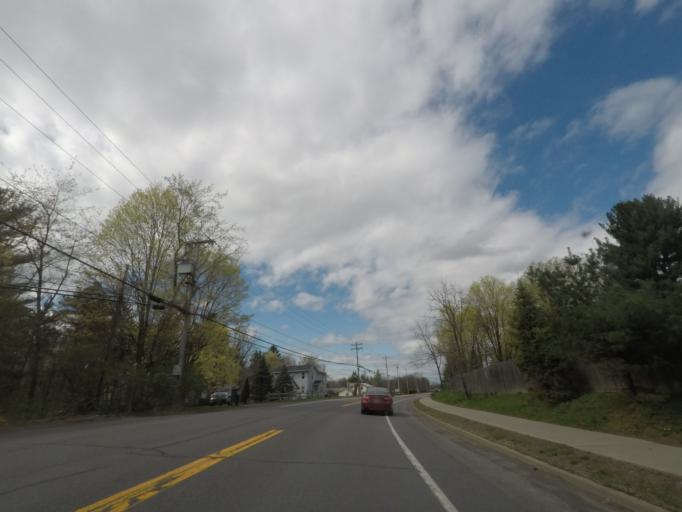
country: US
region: New York
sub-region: Columbia County
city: Valatie
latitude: 42.4169
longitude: -73.6836
